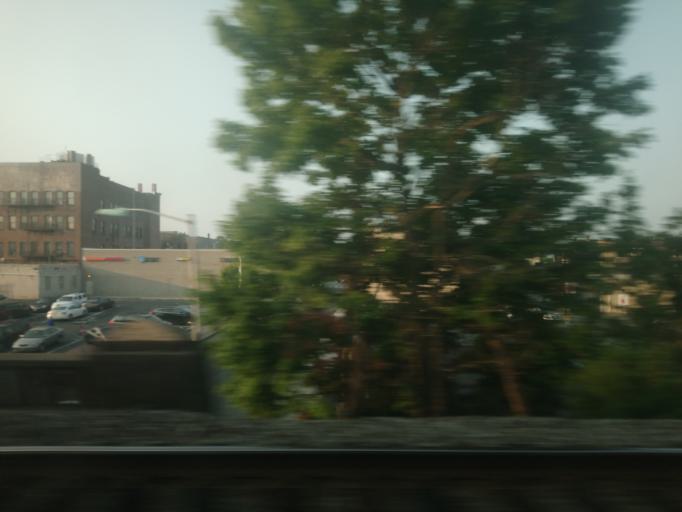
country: US
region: New Jersey
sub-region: Essex County
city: Orange
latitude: 40.7712
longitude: -74.2303
